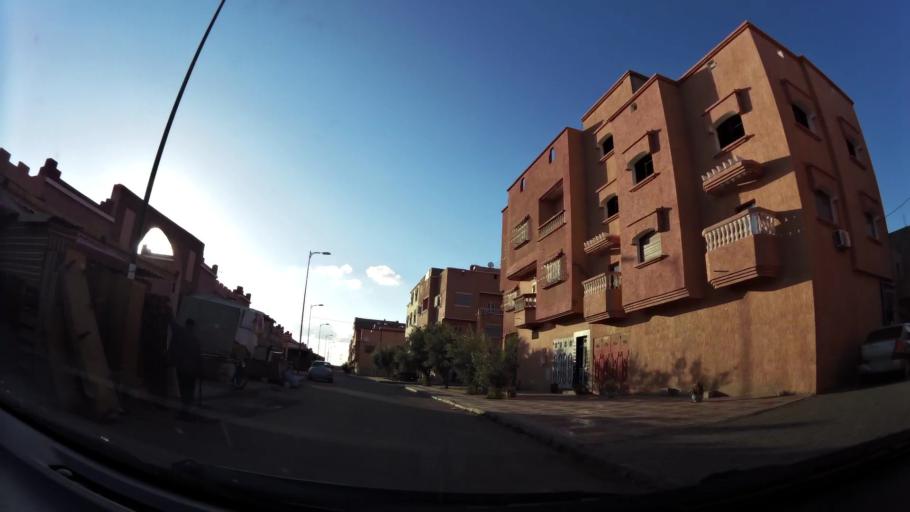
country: MA
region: Marrakech-Tensift-Al Haouz
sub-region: Kelaa-Des-Sraghna
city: Sidi Abdallah
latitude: 32.2383
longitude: -7.9625
